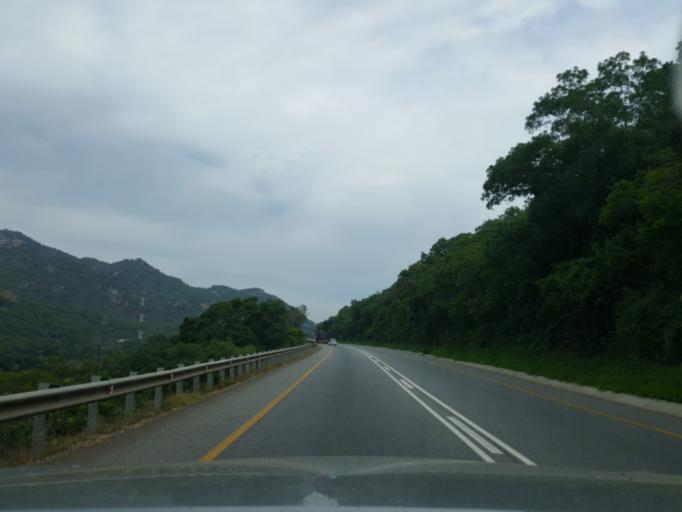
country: ZA
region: Mpumalanga
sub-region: Ehlanzeni District
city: Nelspruit
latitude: -25.5097
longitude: 31.2050
